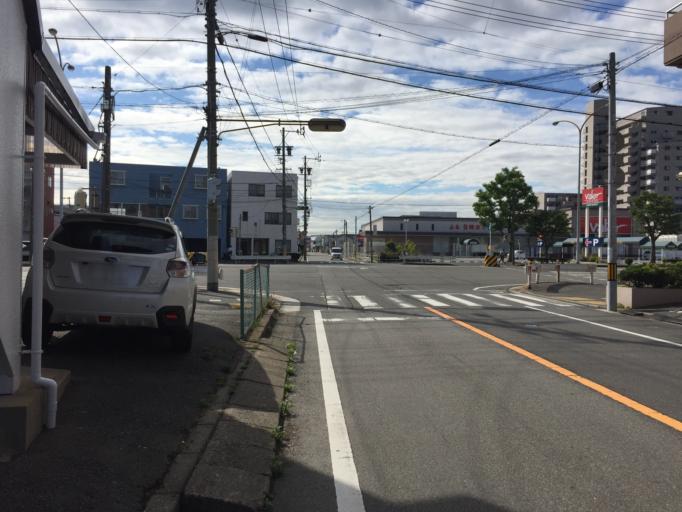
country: JP
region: Mie
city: Yokkaichi
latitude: 34.9615
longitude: 136.6234
